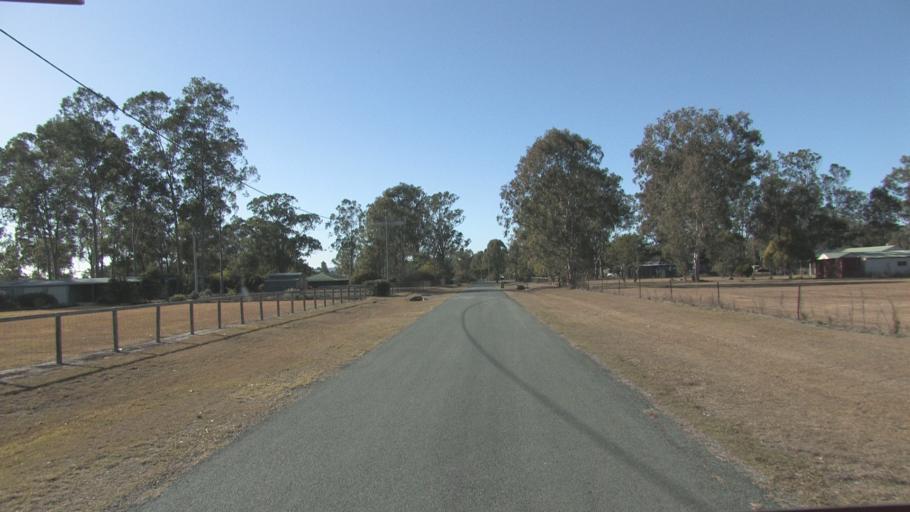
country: AU
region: Queensland
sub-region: Logan
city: North Maclean
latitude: -27.8297
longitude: 152.9906
